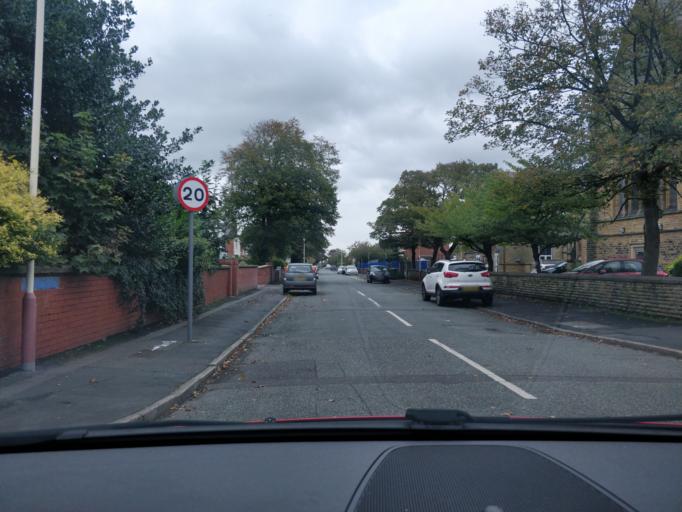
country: GB
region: England
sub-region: Sefton
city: Southport
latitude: 53.6404
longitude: -2.9948
